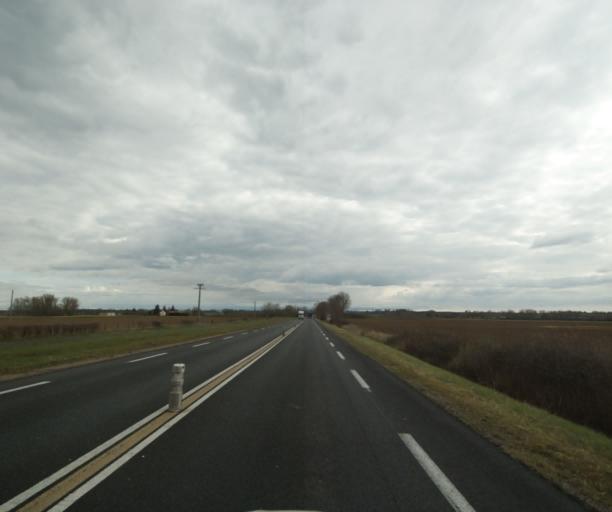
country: FR
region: Auvergne
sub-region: Departement de l'Allier
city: Toulon-sur-Allier
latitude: 46.4854
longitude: 3.3398
